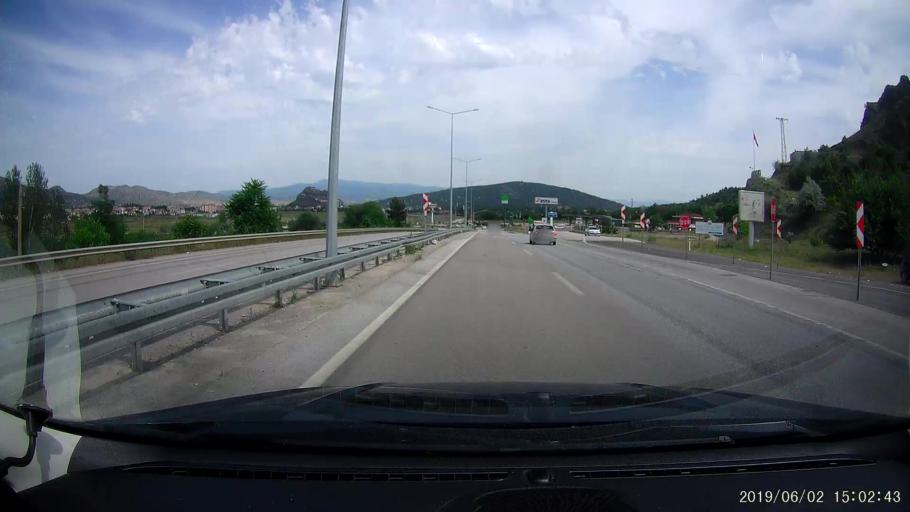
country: TR
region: Corum
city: Osmancik
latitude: 40.9788
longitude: 34.7709
